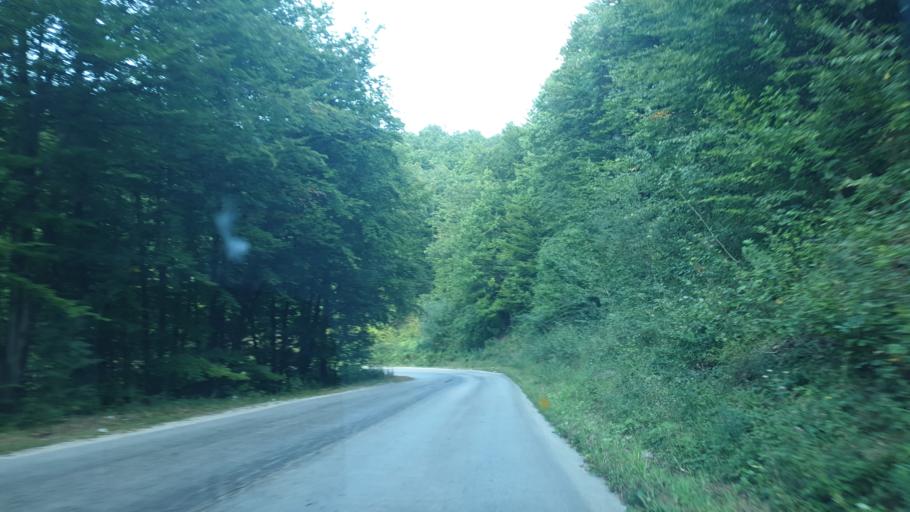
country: RS
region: Central Serbia
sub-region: Zlatiborski Okrug
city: Uzice
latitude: 43.8645
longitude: 19.9066
